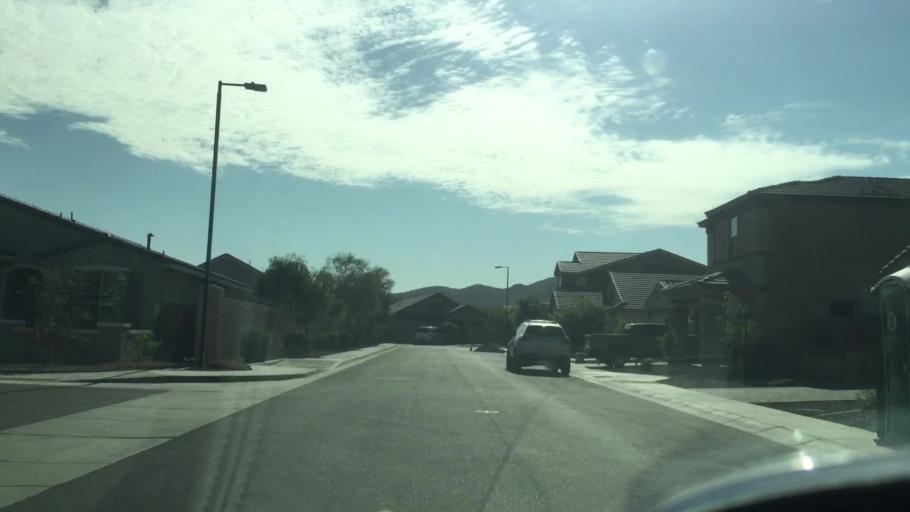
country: US
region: Arizona
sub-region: Maricopa County
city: Guadalupe
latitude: 33.3740
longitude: -112.0292
